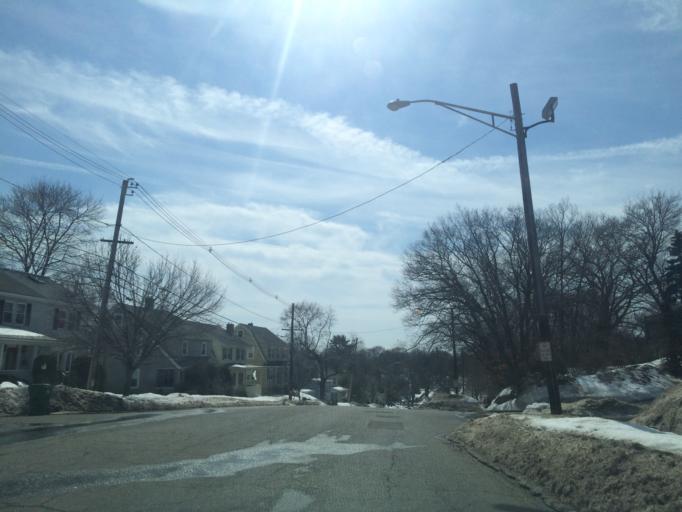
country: US
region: Massachusetts
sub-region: Middlesex County
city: Medford
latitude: 42.4269
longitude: -71.1103
